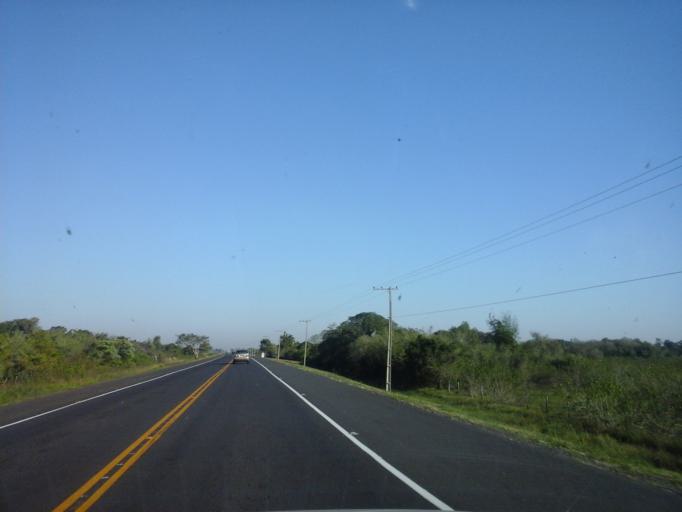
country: PY
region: Neembucu
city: Pilar
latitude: -26.8547
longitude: -58.2005
